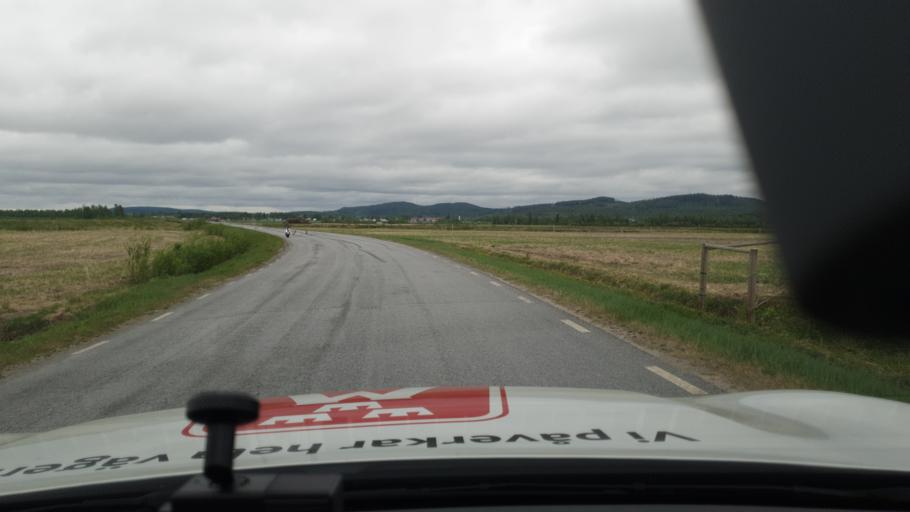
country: SE
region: Vaesterbotten
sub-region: Vannas Kommun
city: Vannasby
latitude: 63.9338
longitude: 19.8340
